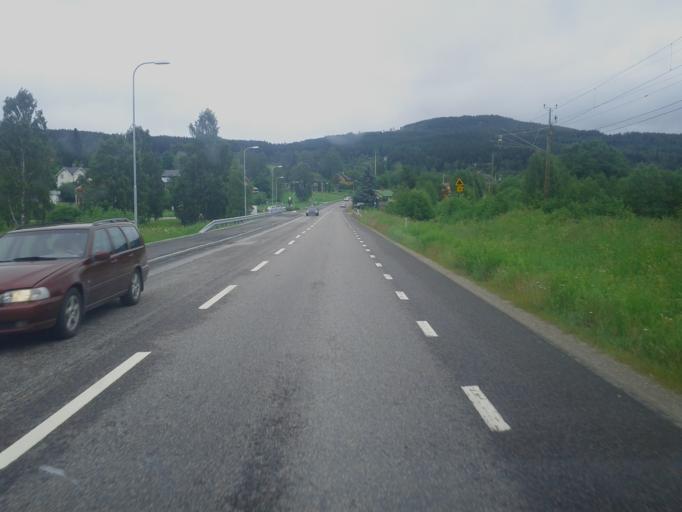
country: SE
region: Vaesternorrland
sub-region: Ange Kommun
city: Fransta
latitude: 62.4186
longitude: 16.5907
